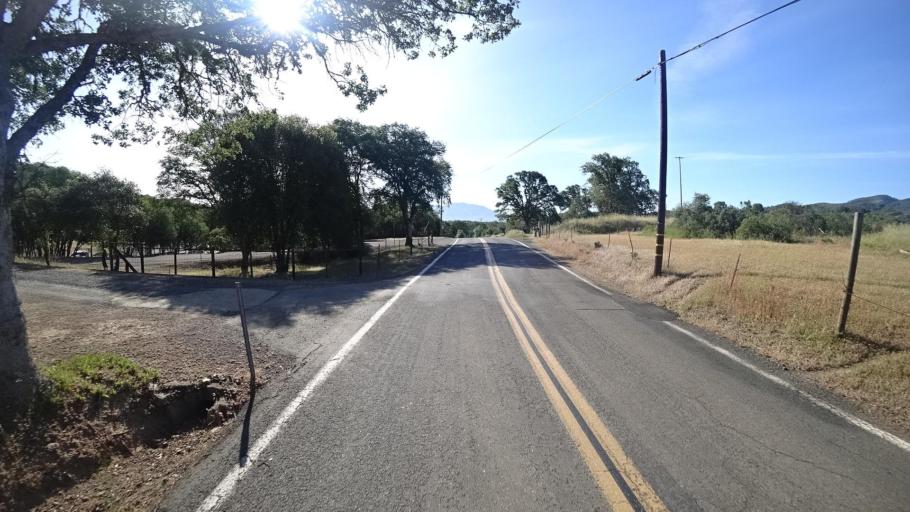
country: US
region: California
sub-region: Lake County
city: Lakeport
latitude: 39.0420
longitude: -122.9466
